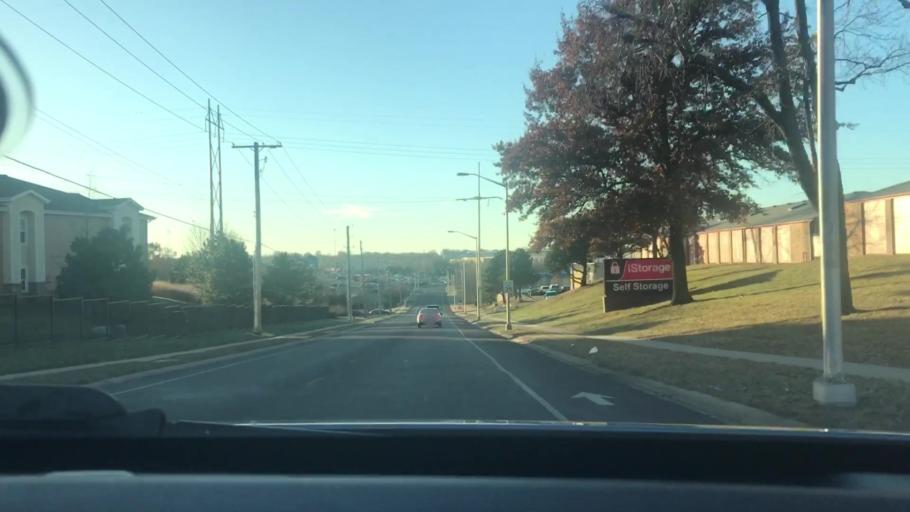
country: US
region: Kansas
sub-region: Johnson County
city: Overland Park
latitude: 38.9858
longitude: -94.6993
